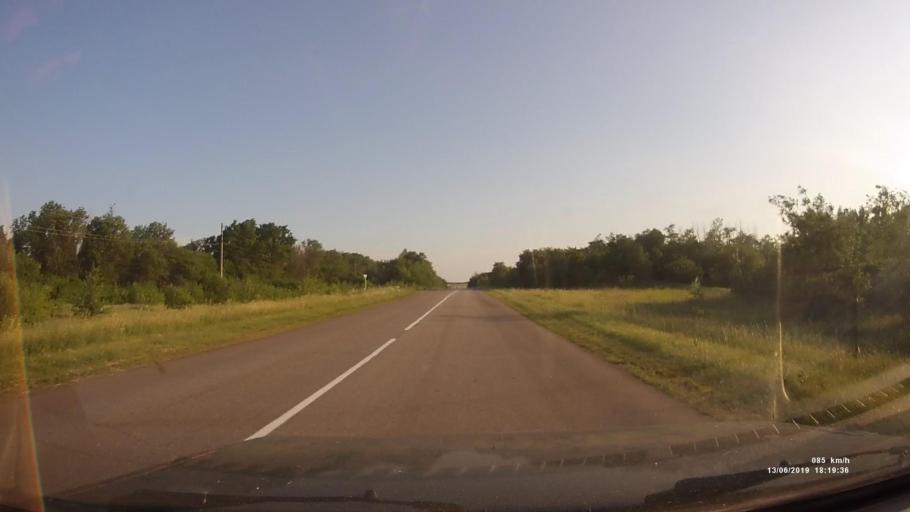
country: RU
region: Rostov
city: Kazanskaya
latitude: 49.8940
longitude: 41.3053
